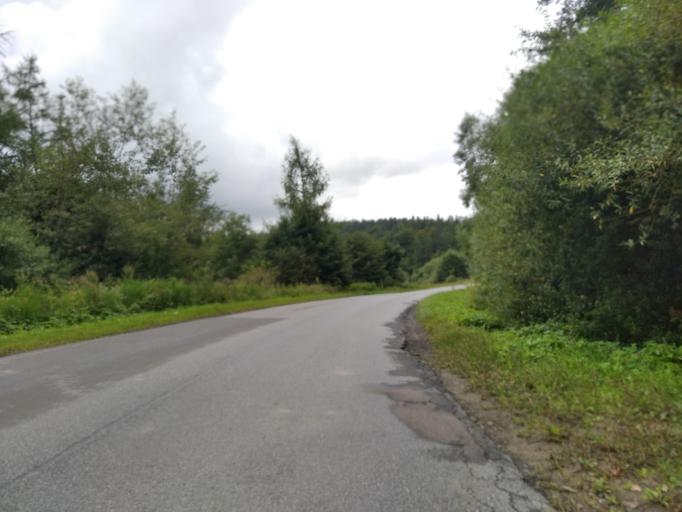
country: PL
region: Subcarpathian Voivodeship
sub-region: Powiat przemyski
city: Bircza
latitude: 49.6906
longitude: 22.4187
